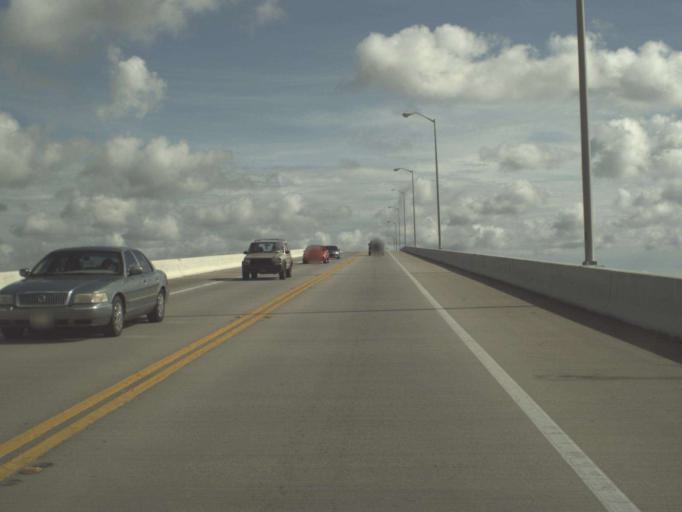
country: US
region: Florida
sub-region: Gulf County
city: Port Saint Joe
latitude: 29.8342
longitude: -85.3146
